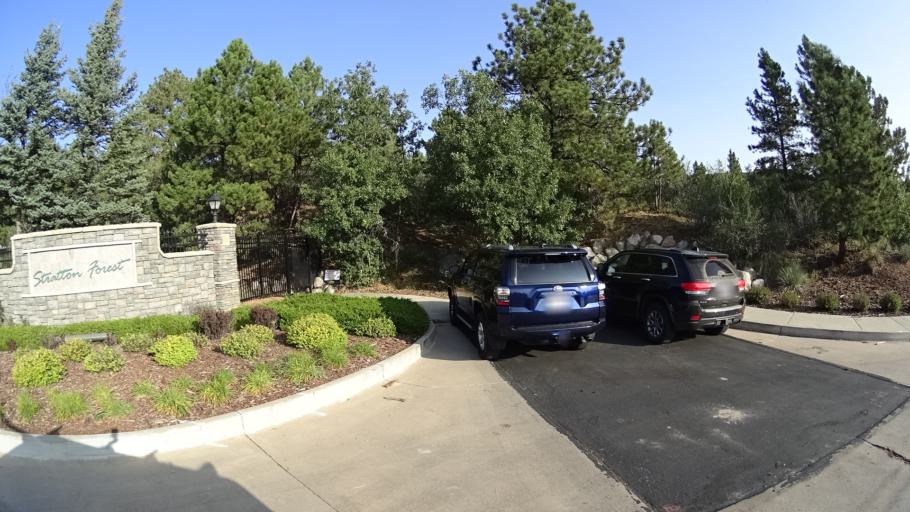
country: US
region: Colorado
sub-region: El Paso County
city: Colorado Springs
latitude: 38.8043
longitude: -104.8625
